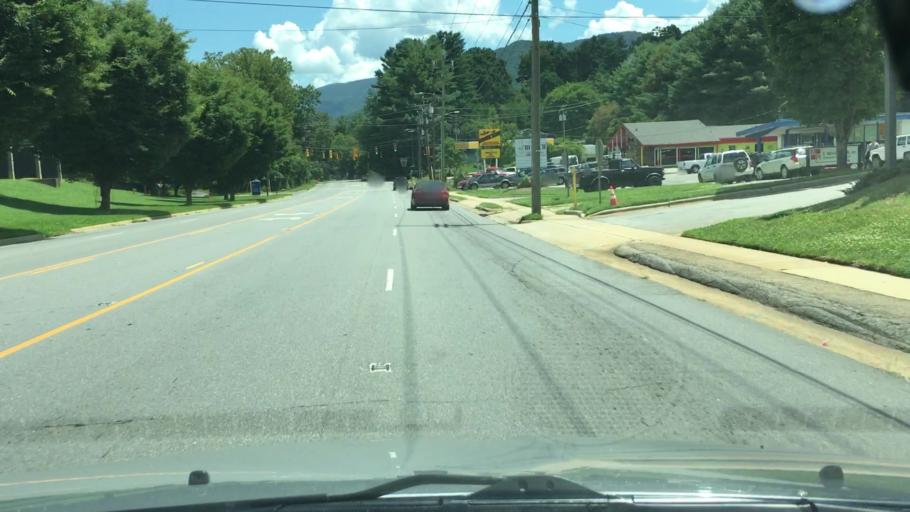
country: US
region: North Carolina
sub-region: Buncombe County
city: Biltmore Forest
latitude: 35.5869
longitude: -82.4840
